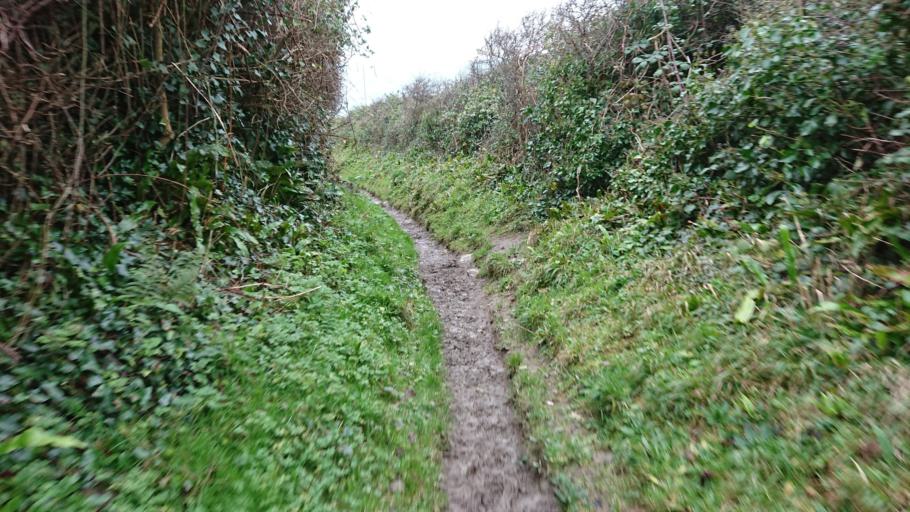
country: GB
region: England
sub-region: Cornwall
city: Fowey
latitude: 50.3334
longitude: -4.5774
